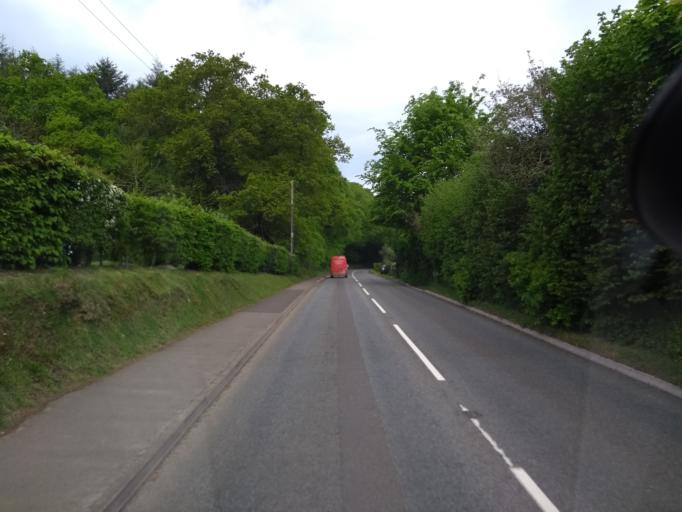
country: GB
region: England
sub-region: Dorset
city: Lyme Regis
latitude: 50.7425
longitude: -2.9200
